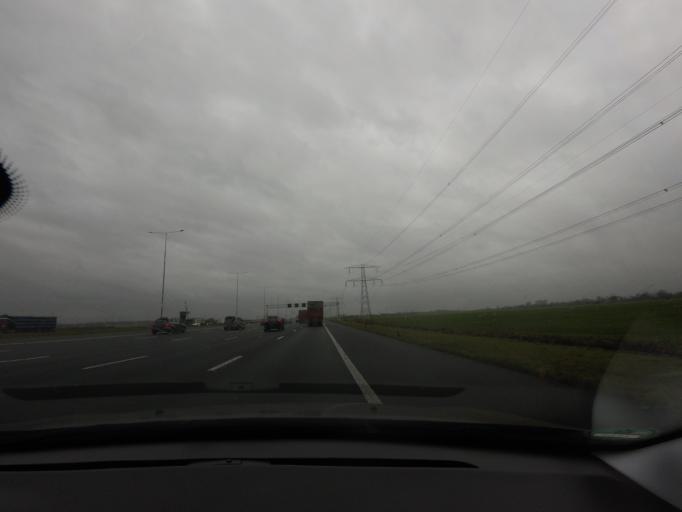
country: NL
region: Utrecht
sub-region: Stichtse Vecht
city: Breukelen
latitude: 52.2081
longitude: 4.9849
